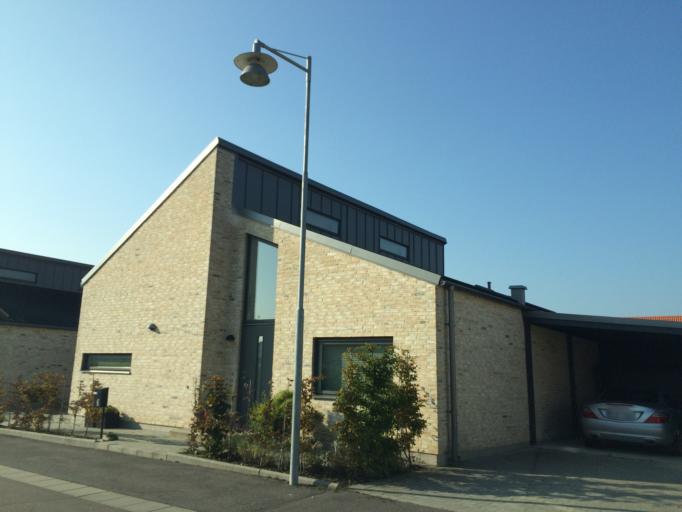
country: SE
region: Skane
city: Bjarred
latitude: 55.7328
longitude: 13.0381
